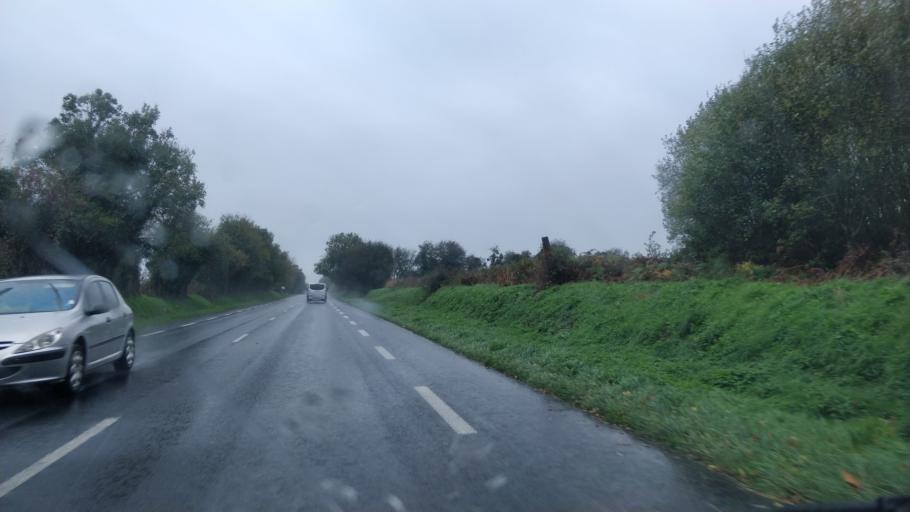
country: FR
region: Lower Normandy
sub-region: Departement de la Manche
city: Brehal
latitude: 48.8733
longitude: -1.5361
